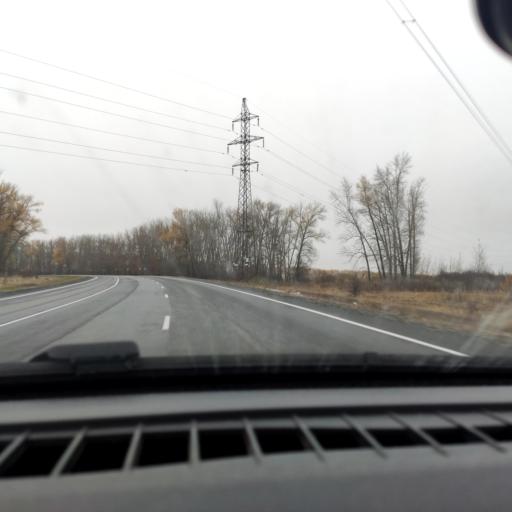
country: RU
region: Voronezj
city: Ostrogozhsk
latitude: 50.9456
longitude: 39.0545
